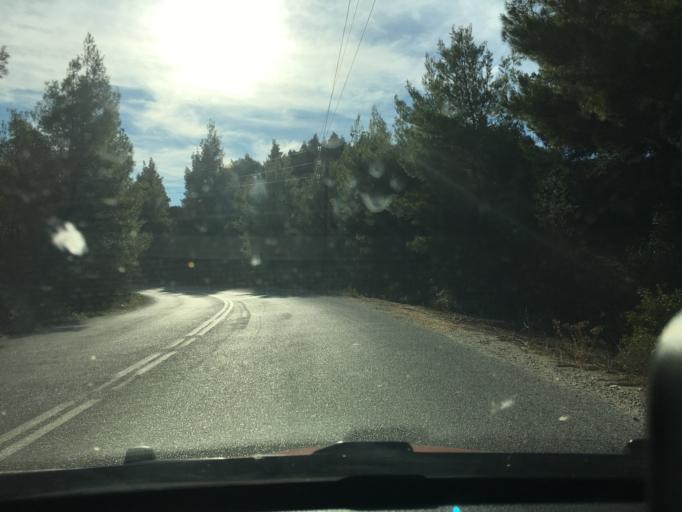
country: GR
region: Central Macedonia
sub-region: Nomos Chalkidikis
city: Agios Nikolaos
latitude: 40.2787
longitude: 23.6826
